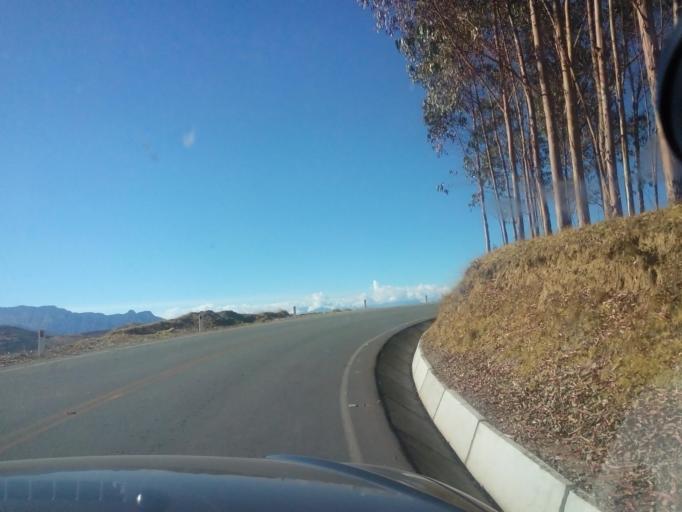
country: PE
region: Apurimac
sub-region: Provincia de Andahuaylas
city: Pacucha
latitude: -13.6543
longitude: -73.2919
